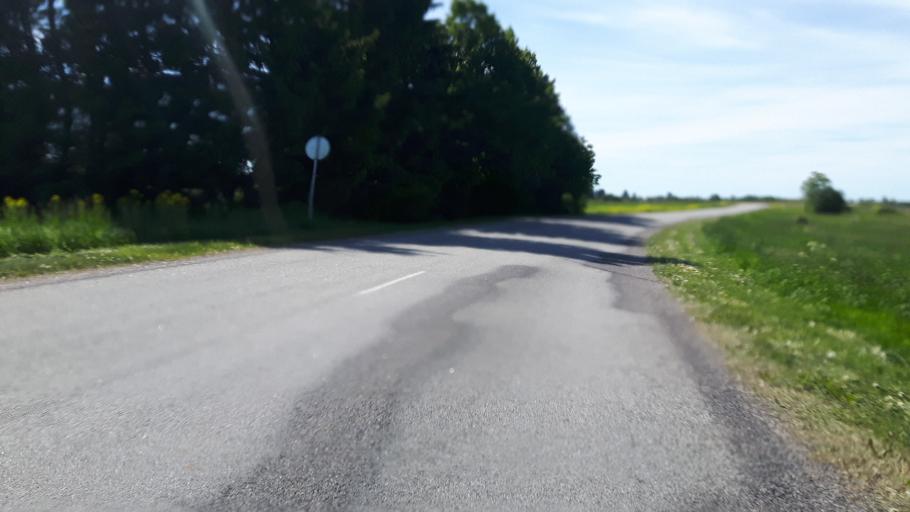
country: EE
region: Harju
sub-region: Kuusalu vald
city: Kuusalu
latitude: 59.4517
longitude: 25.3763
